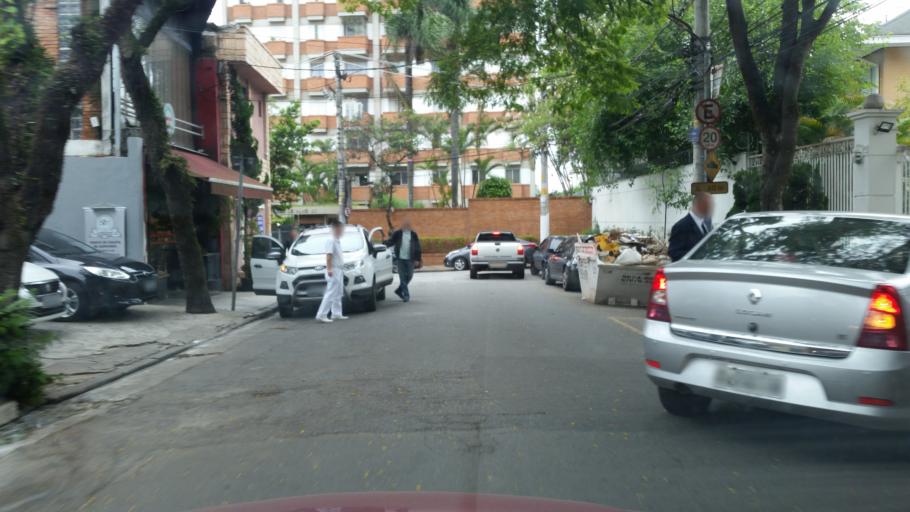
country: BR
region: Sao Paulo
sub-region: Diadema
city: Diadema
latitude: -23.6592
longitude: -46.6926
